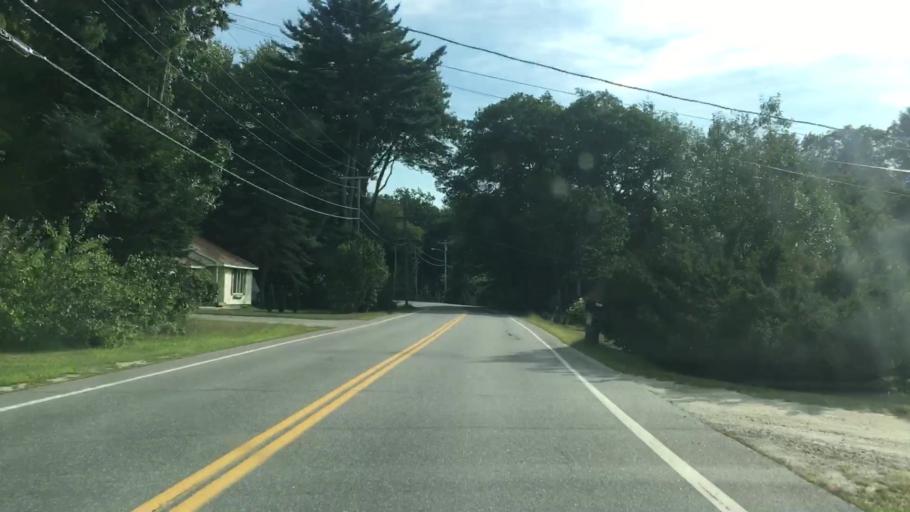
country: US
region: Maine
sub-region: Cumberland County
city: Brunswick
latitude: 43.9236
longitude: -69.8969
